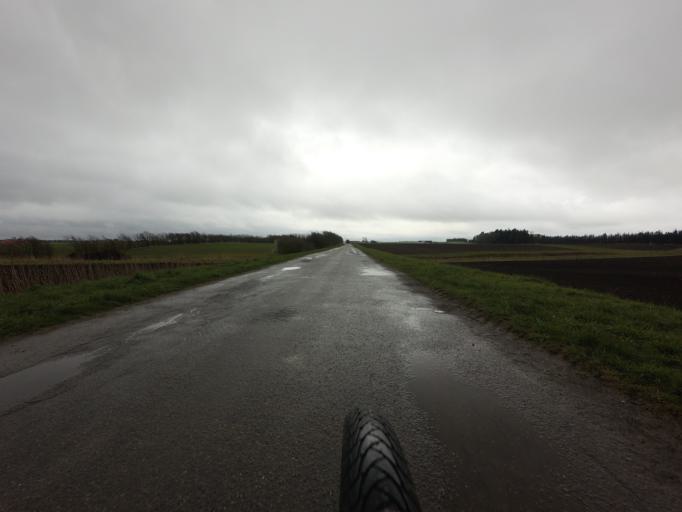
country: DK
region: North Denmark
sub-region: Hjorring Kommune
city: Vra
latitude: 57.3851
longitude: 9.8383
